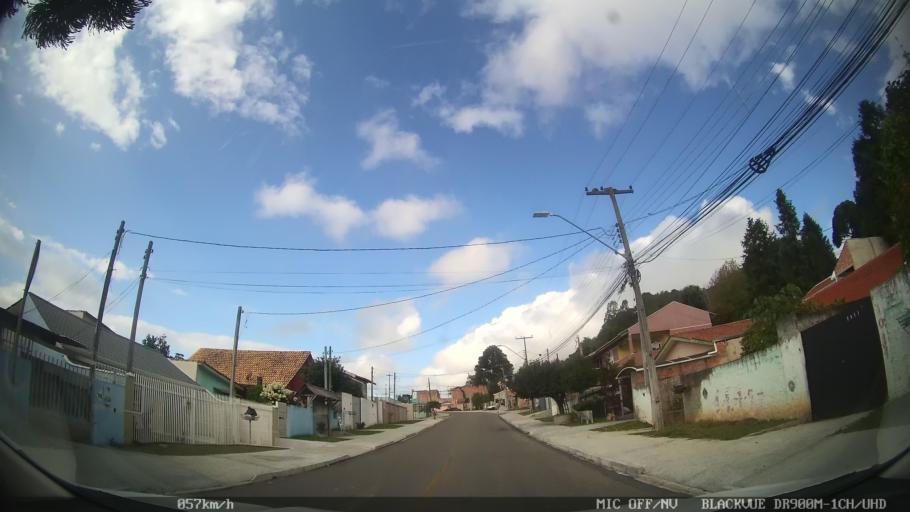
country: BR
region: Parana
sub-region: Pinhais
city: Pinhais
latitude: -25.3962
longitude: -49.1838
